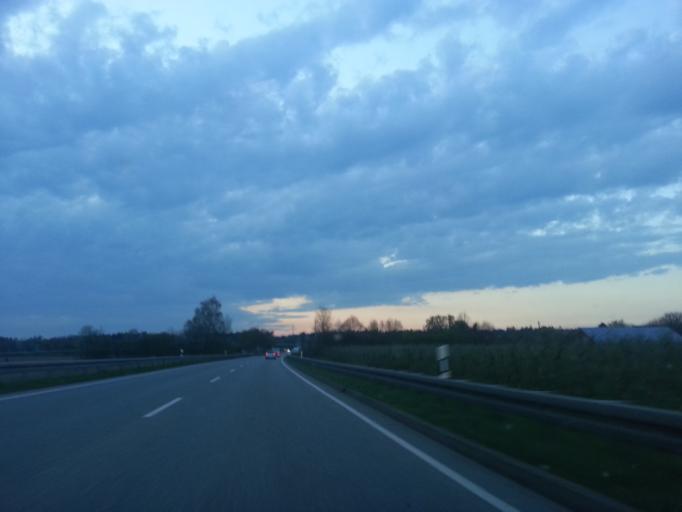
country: DE
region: Baden-Wuerttemberg
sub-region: Tuebingen Region
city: Kressbronn am Bodensee
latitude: 47.6116
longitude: 9.5724
